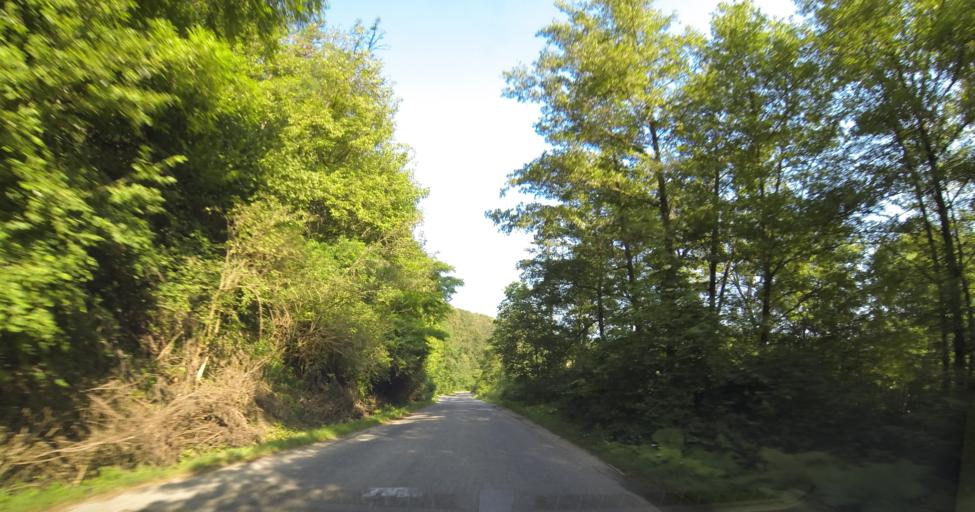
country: RO
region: Valcea
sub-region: Comuna Maldaresti
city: Maldaresti
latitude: 45.1116
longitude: 24.0037
